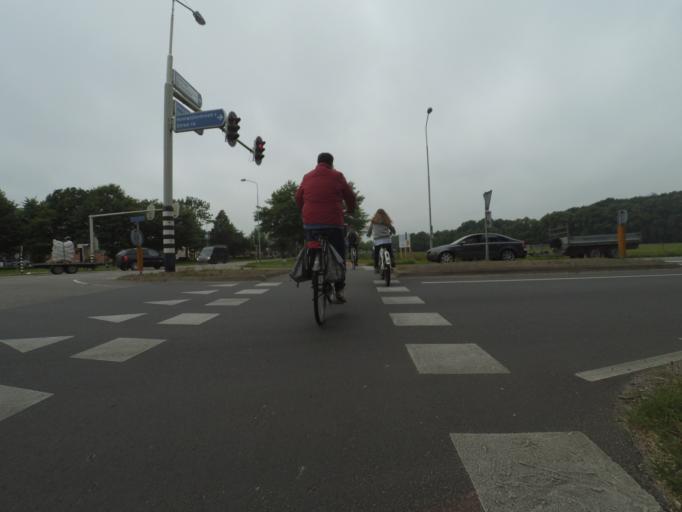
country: NL
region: Gelderland
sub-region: Gemeente Barneveld
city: Barneveld
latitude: 52.1397
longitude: 5.5968
